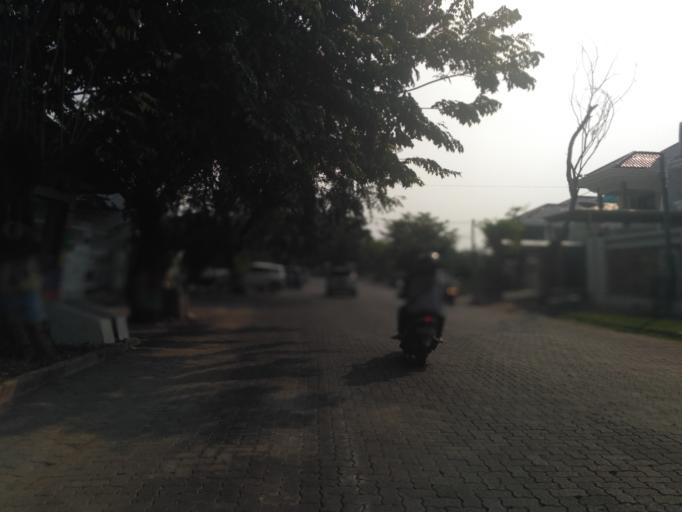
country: ID
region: Central Java
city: Semarang
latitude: -6.9678
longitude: 110.3876
